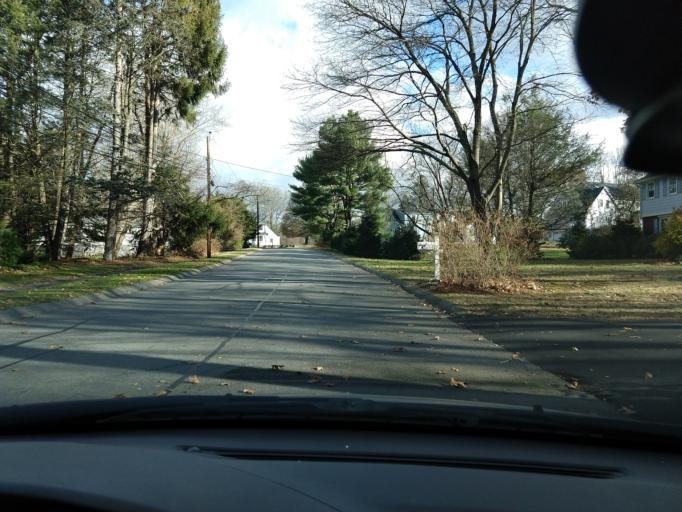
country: US
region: Massachusetts
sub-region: Middlesex County
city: Bedford
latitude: 42.4876
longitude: -71.2444
